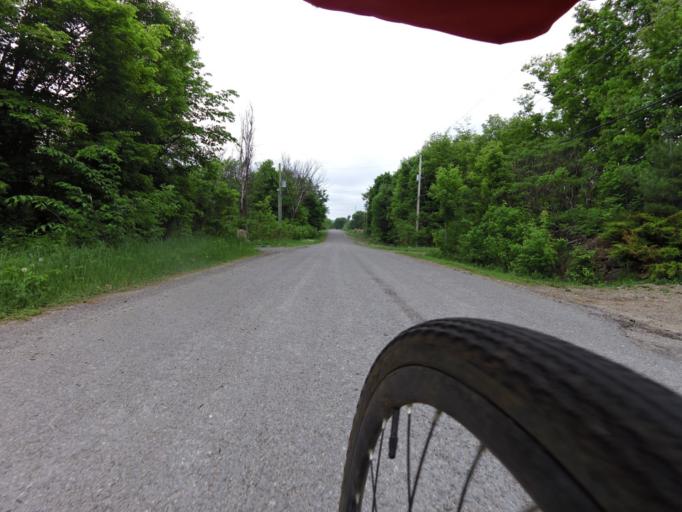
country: CA
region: Ontario
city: Renfrew
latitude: 45.2927
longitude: -76.7216
